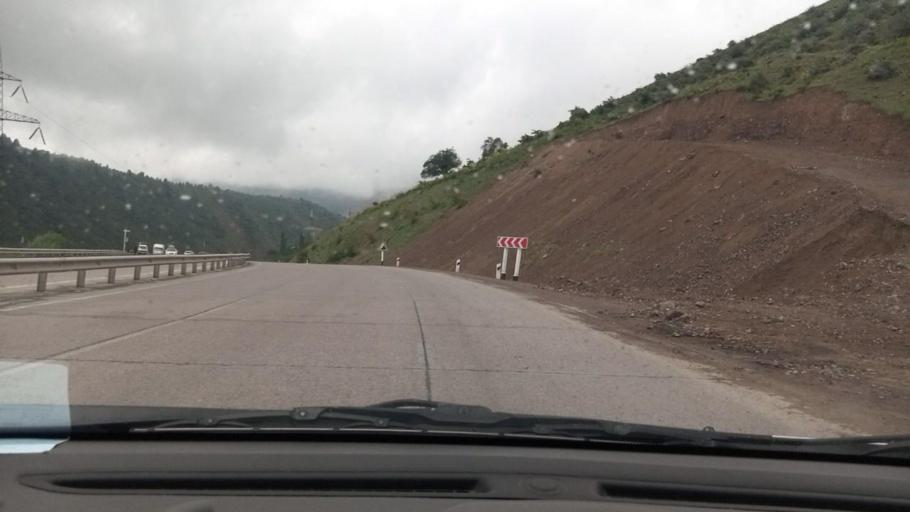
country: UZ
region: Toshkent
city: Angren
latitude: 41.1379
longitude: 70.4591
